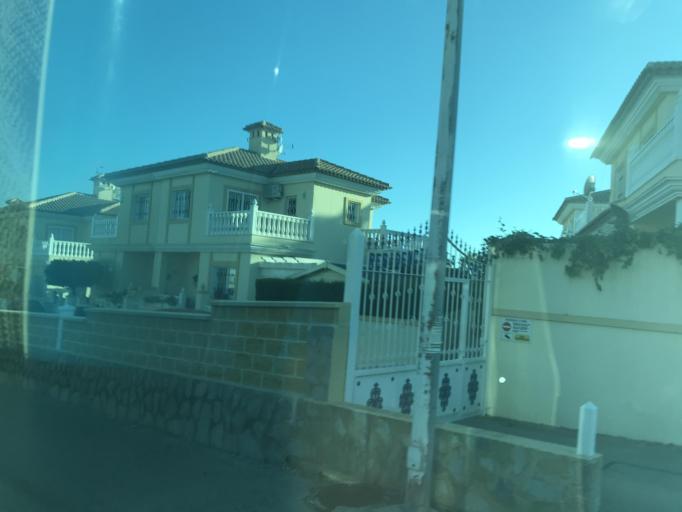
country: ES
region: Valencia
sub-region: Provincia de Alicante
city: Torrevieja
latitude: 38.0019
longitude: -0.6527
